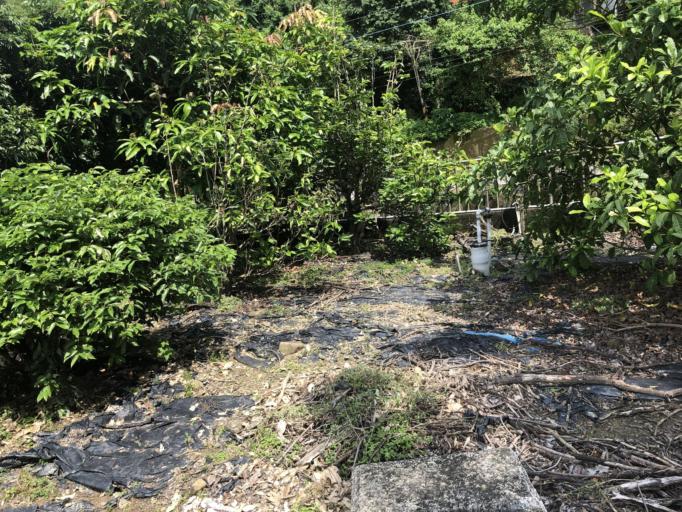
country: TW
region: Taiwan
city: Yujing
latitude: 22.9337
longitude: 120.5870
